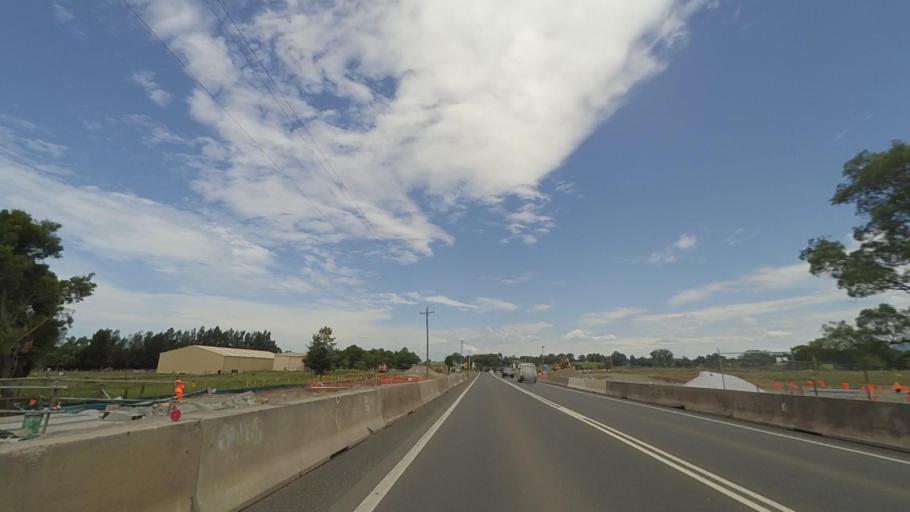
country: AU
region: New South Wales
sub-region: Shoalhaven Shire
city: Berry
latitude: -34.7859
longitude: 150.6759
